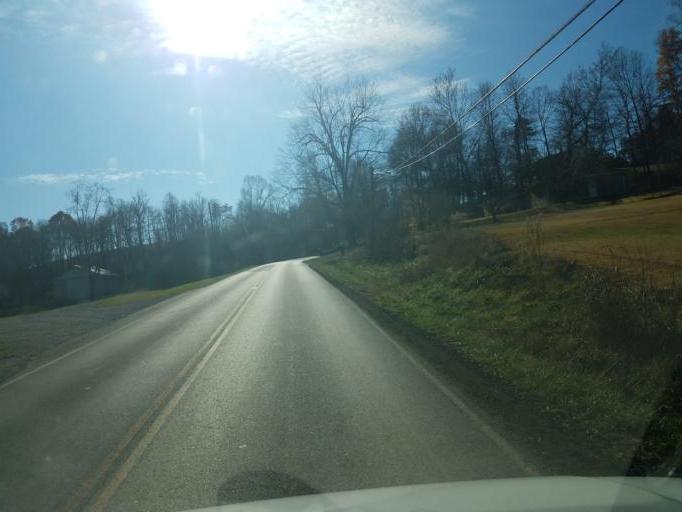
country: US
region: Ohio
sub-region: Scioto County
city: Sciotodale
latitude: 38.7844
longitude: -82.8516
